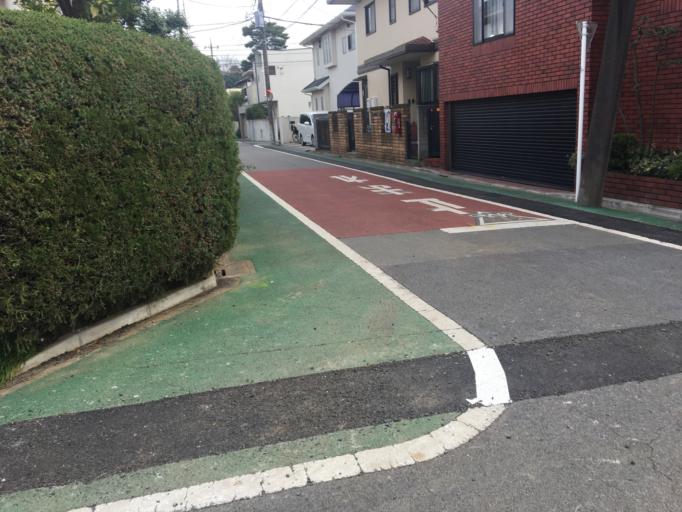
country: JP
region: Tokyo
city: Musashino
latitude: 35.6992
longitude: 139.5681
